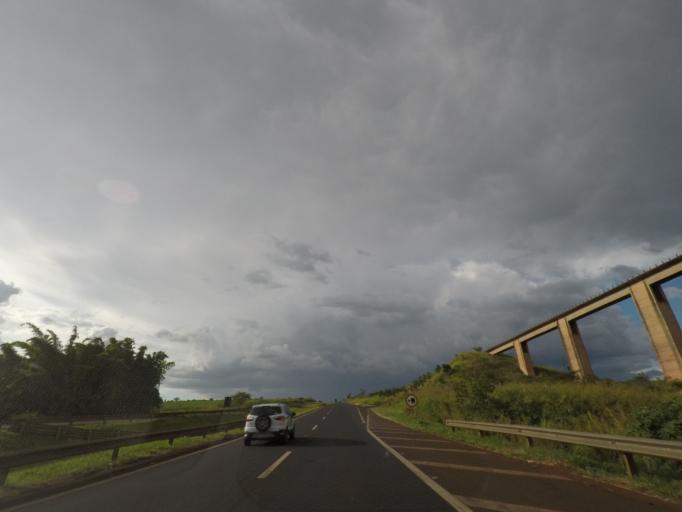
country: BR
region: Sao Paulo
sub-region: Jardinopolis
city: Jardinopolis
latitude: -21.0078
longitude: -47.8465
